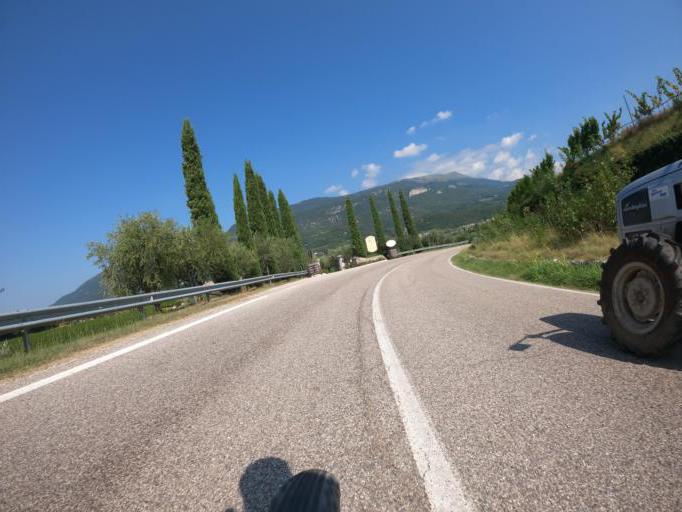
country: IT
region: Veneto
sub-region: Provincia di Verona
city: Caprino Veronese
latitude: 45.5988
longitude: 10.8138
